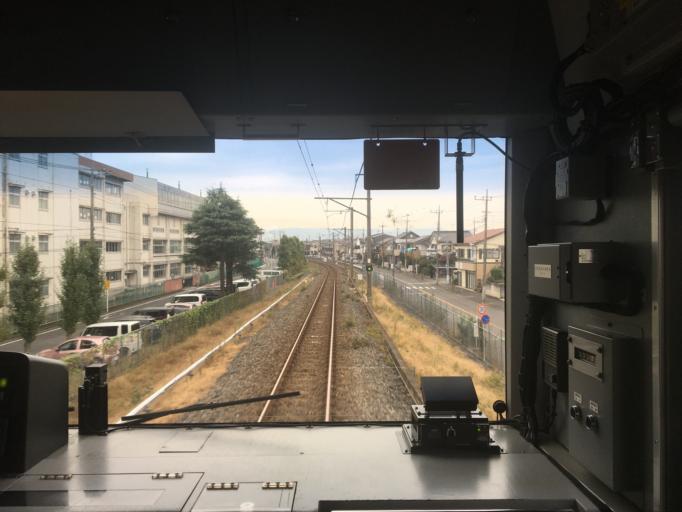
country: JP
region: Saitama
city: Kawagoe
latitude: 35.9209
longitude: 139.4501
